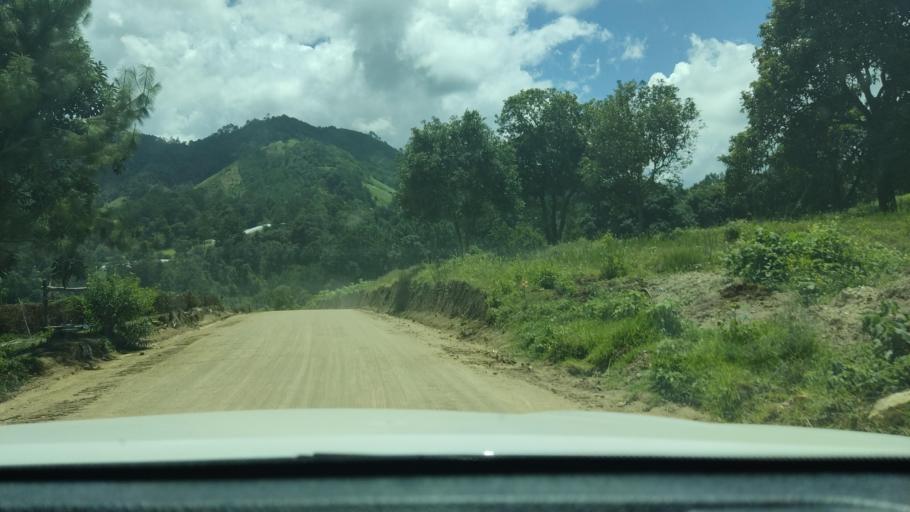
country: GT
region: Chimaltenango
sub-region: Municipio de San Juan Comalapa
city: Comalapa
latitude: 14.7646
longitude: -90.8829
